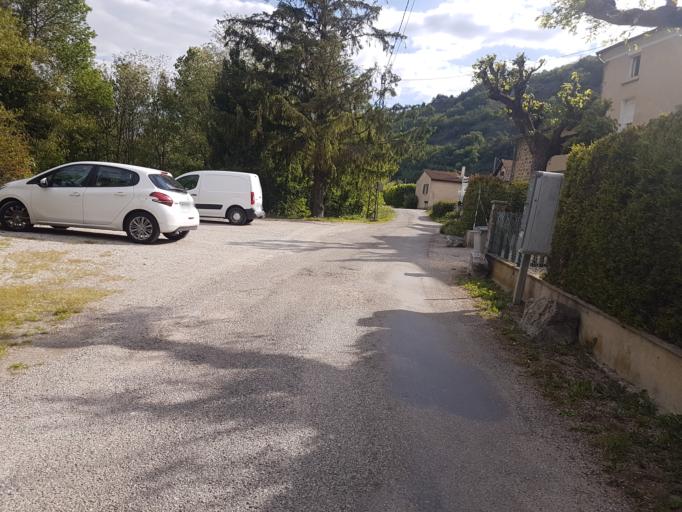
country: FR
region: Rhone-Alpes
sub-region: Departement de l'Ardeche
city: Soyons
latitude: 44.9109
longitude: 4.8555
